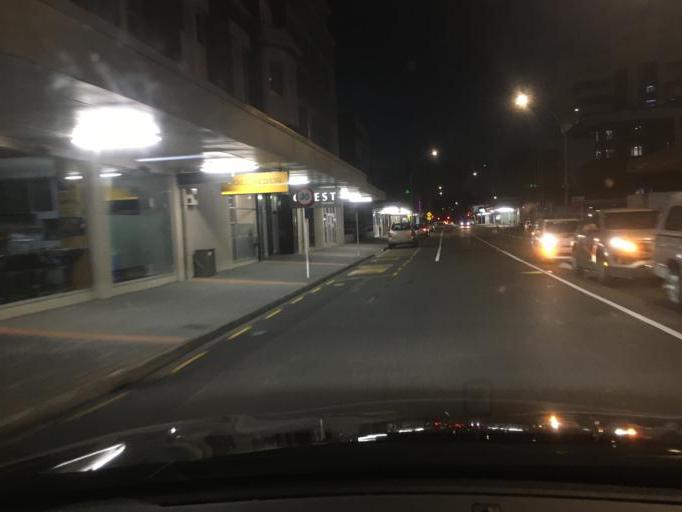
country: NZ
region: Waikato
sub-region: Hamilton City
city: Hamilton
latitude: -37.7833
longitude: 175.2792
